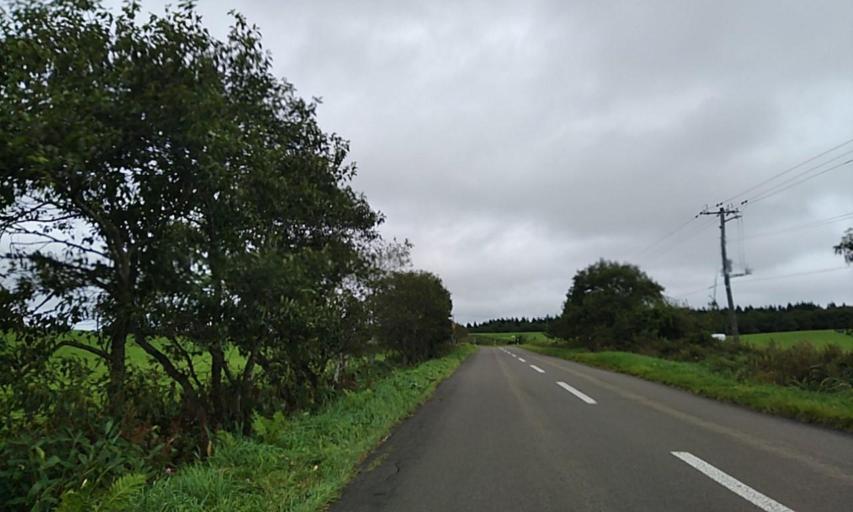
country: JP
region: Hokkaido
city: Nemuro
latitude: 43.2646
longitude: 145.2641
